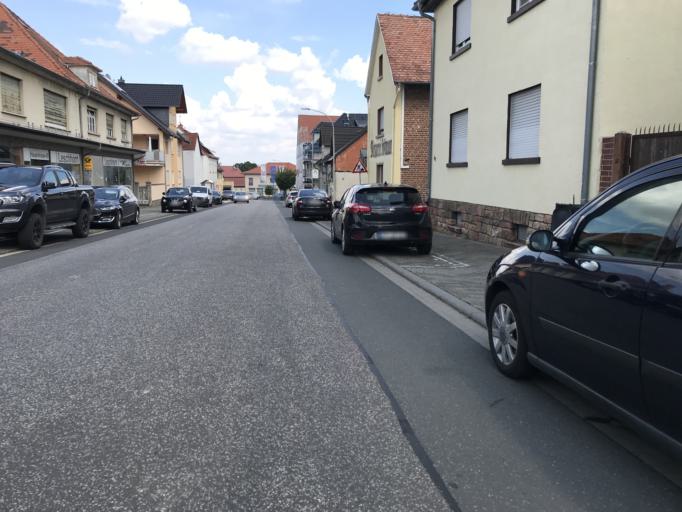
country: DE
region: Hesse
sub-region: Regierungsbezirk Darmstadt
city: Wolfersheim
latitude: 50.3977
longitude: 8.8116
